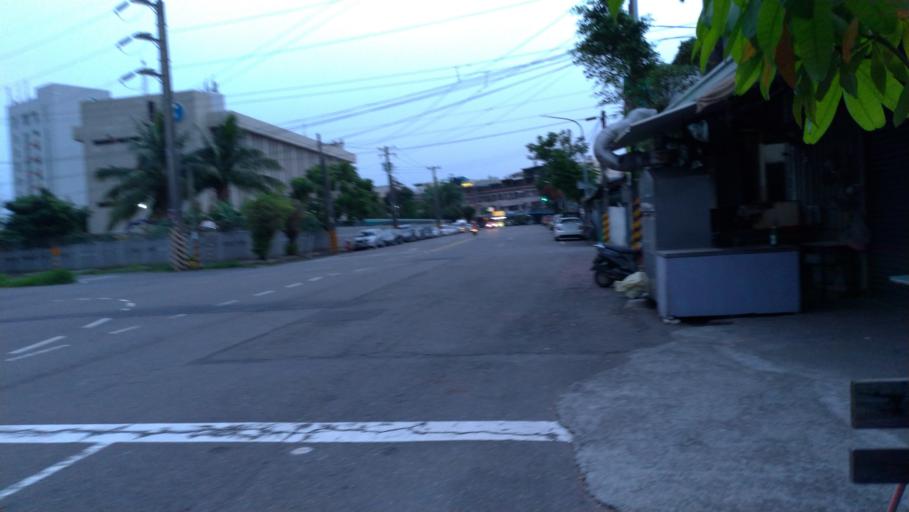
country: TW
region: Taiwan
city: Fengshan
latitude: 22.6551
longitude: 120.3621
